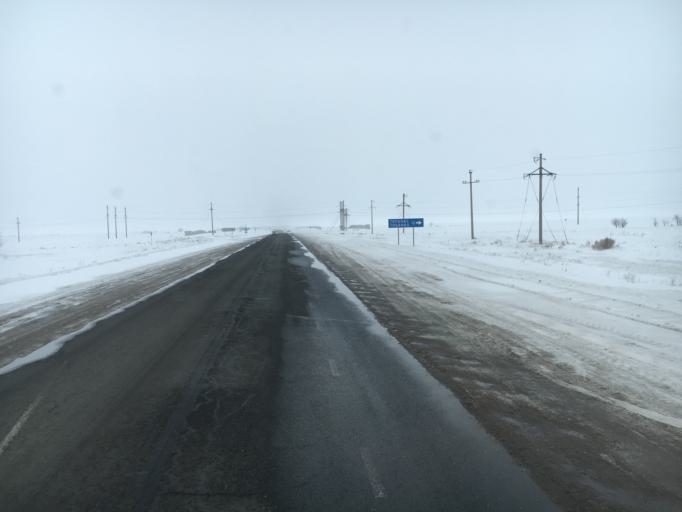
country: KZ
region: Batys Qazaqstan
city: Fedorovka
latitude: 50.7615
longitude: 51.9131
